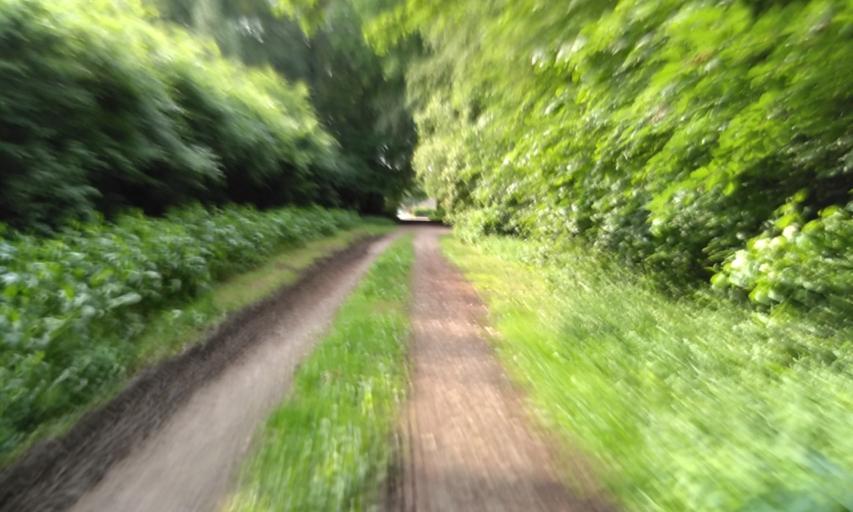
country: DE
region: Lower Saxony
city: Nottensdorf
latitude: 53.4765
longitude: 9.6198
